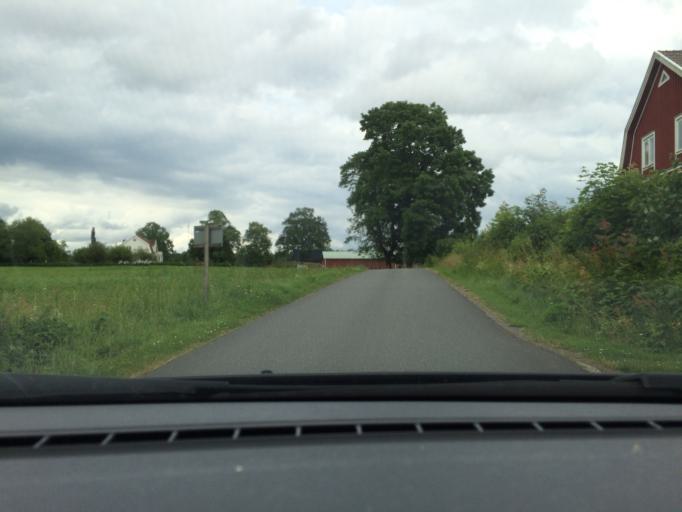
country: SE
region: Joenkoeping
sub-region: Varnamo Kommun
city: Varnamo
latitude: 57.1859
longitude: 13.9358
